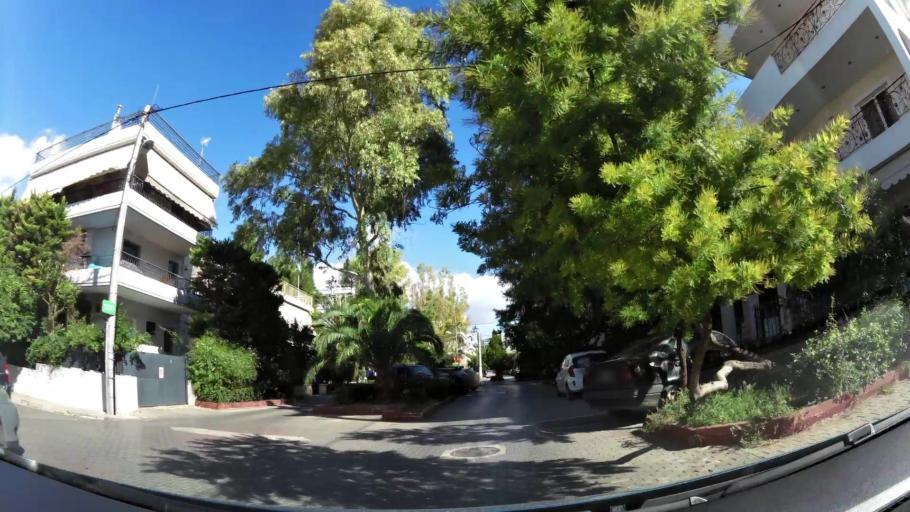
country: GR
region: Attica
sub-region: Nomarchia Athinas
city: Neo Psychiko
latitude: 38.0034
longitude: 23.7871
